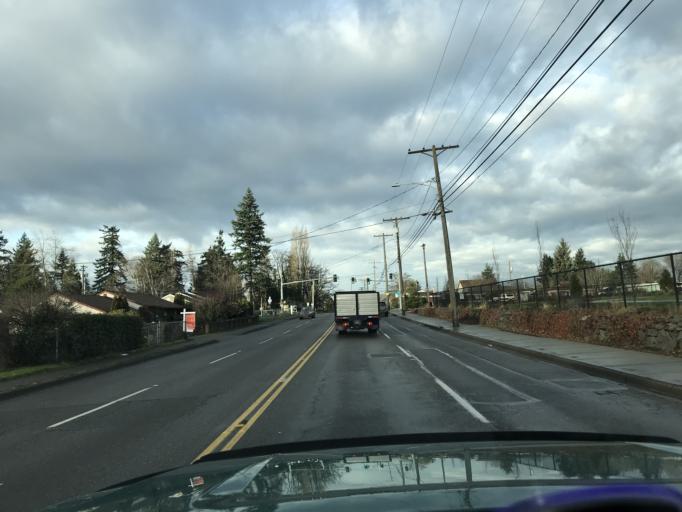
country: US
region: Washington
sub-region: Pierce County
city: Lakewood
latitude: 47.1902
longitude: -122.4743
